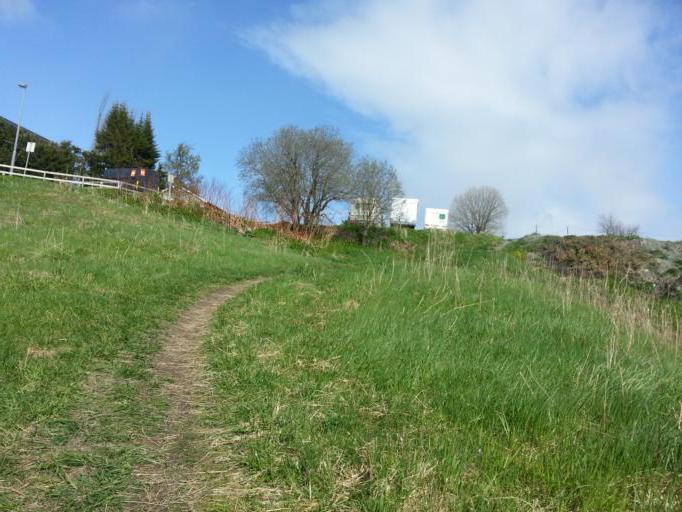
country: NO
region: Sor-Trondelag
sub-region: Trondheim
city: Trondheim
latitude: 63.3934
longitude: 10.3575
